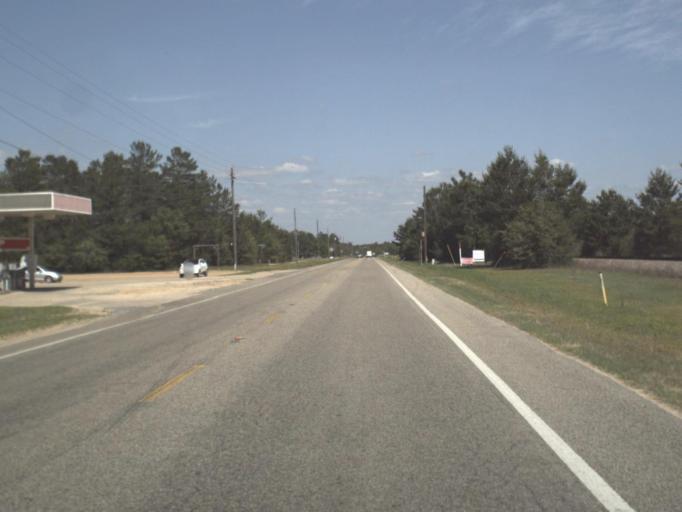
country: US
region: Florida
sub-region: Okaloosa County
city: Crestview
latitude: 30.7513
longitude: -86.4451
